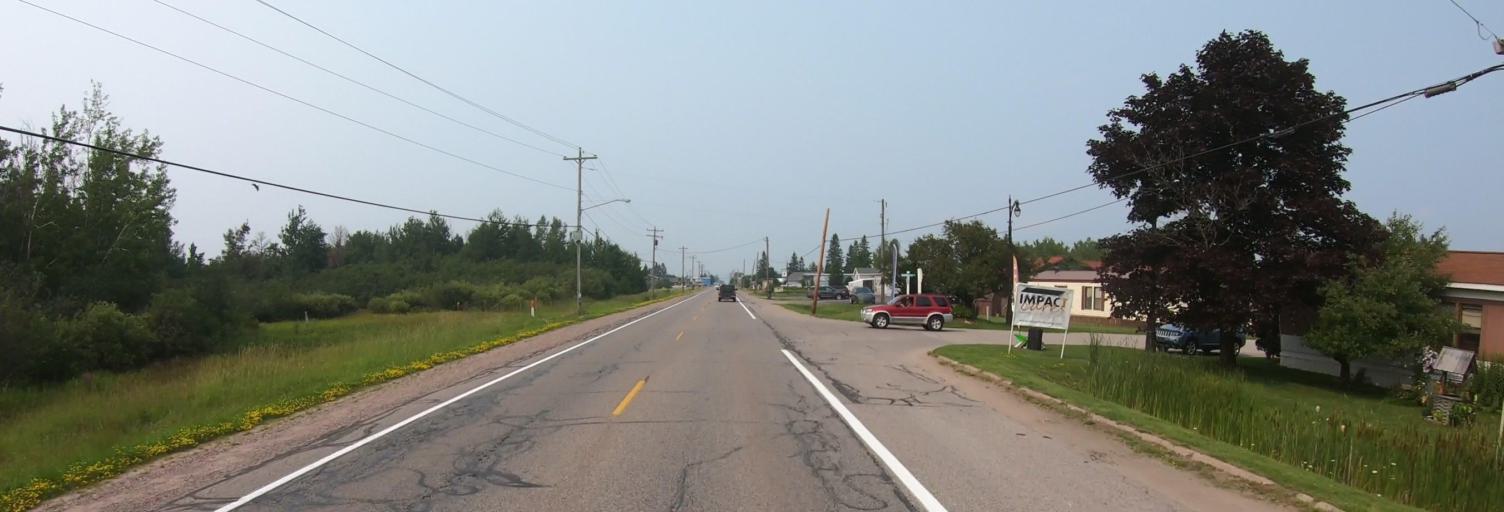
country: US
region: Michigan
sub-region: Chippewa County
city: Sault Ste. Marie
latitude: 46.4690
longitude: -84.3549
